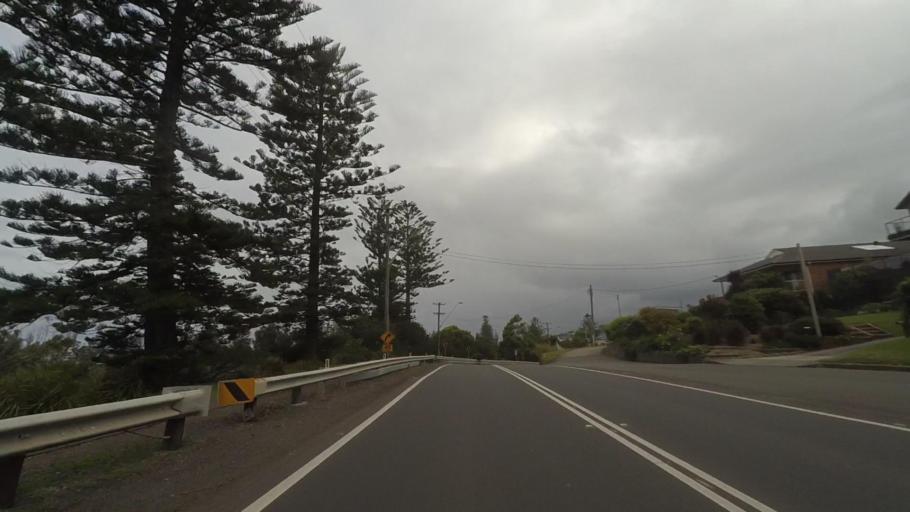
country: AU
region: New South Wales
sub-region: Wollongong
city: Bulli
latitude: -34.2991
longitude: 150.9405
